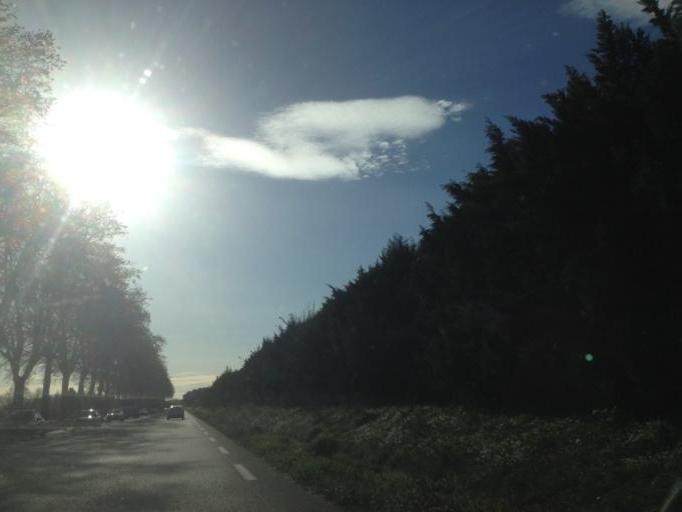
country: FR
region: Provence-Alpes-Cote d'Azur
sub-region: Departement du Vaucluse
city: Courthezon
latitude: 44.0724
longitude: 4.8834
